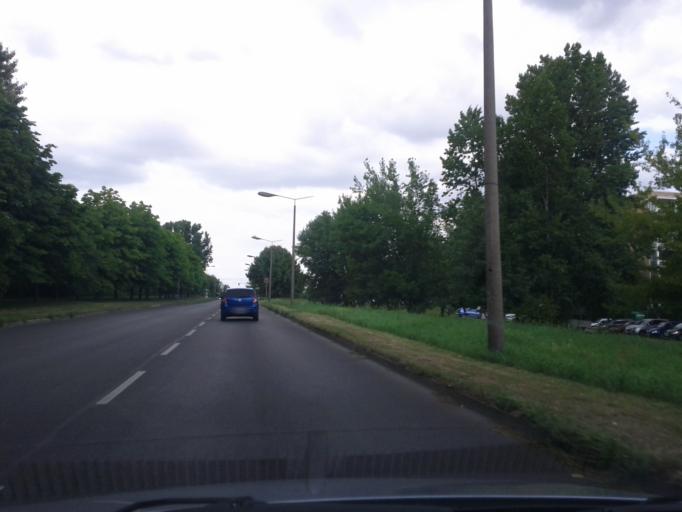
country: DE
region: Berlin
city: Marzahn
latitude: 52.5528
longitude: 13.5738
